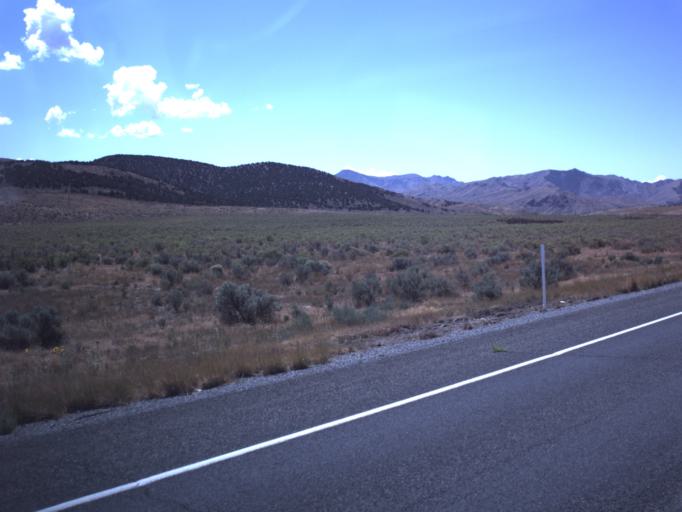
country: US
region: Utah
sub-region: Juab County
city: Nephi
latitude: 39.6315
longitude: -112.1154
